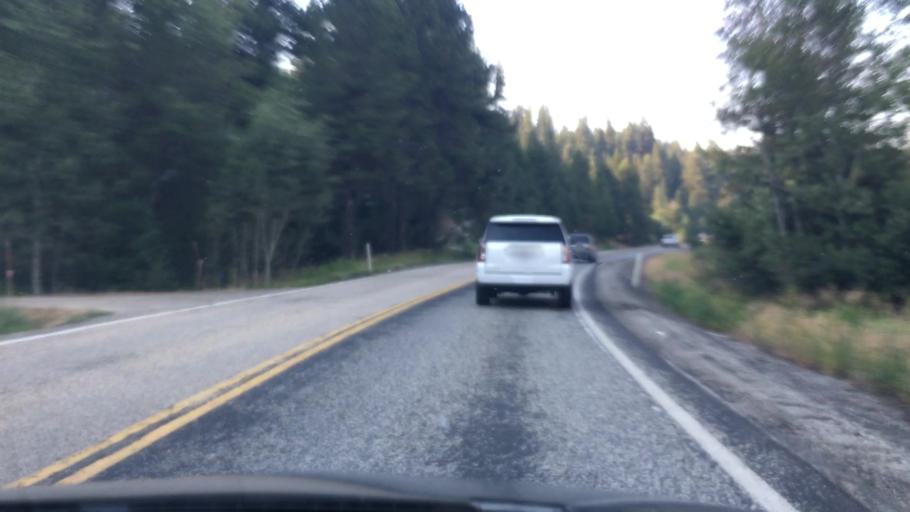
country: US
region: Idaho
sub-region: Valley County
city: Cascade
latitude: 44.3076
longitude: -116.0875
